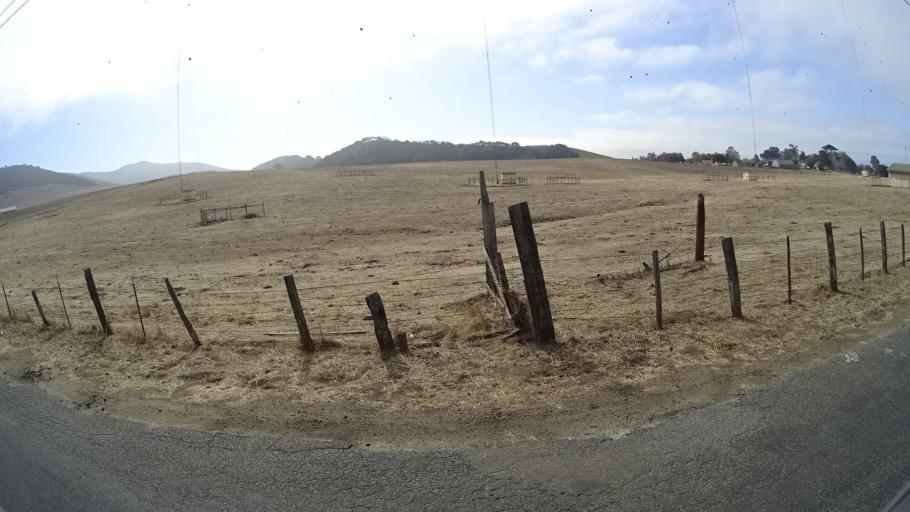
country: US
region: California
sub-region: Monterey County
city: Salinas
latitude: 36.7336
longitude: -121.5925
